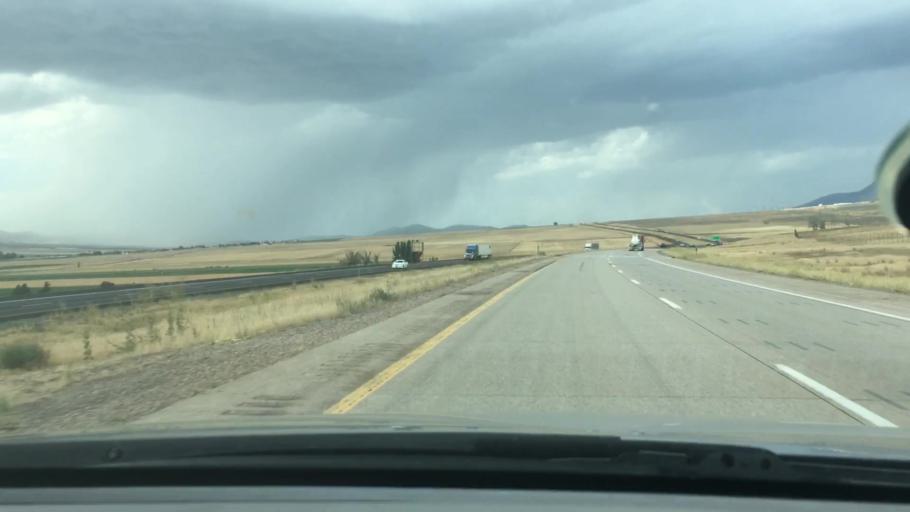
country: US
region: Utah
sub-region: Juab County
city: Mona
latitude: 39.7701
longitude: -111.8398
